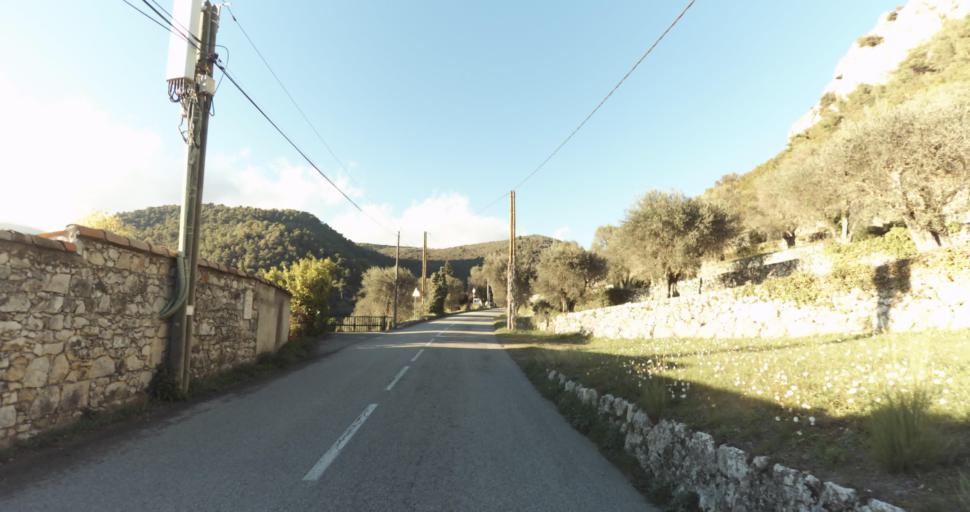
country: FR
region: Provence-Alpes-Cote d'Azur
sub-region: Departement des Alpes-Maritimes
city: Vence
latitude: 43.7320
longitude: 7.1064
